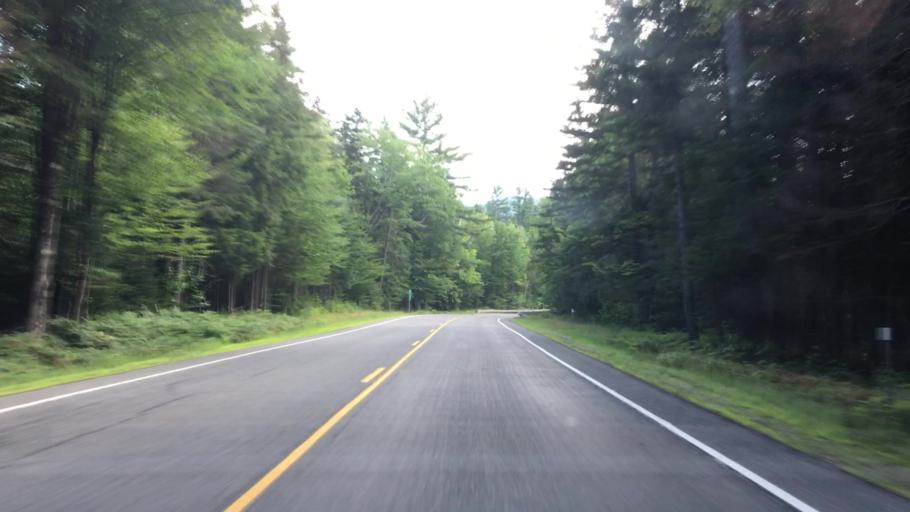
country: US
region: New Hampshire
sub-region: Grafton County
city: Woodstock
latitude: 44.0727
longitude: -71.7939
